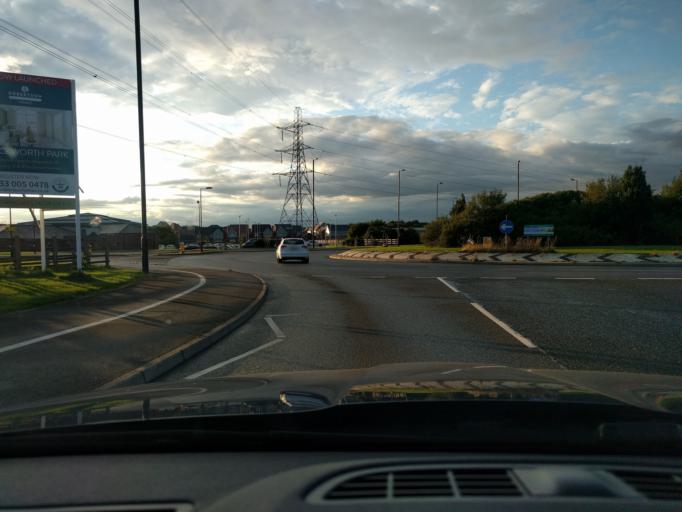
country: GB
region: England
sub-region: Northumberland
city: Backworth
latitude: 55.0339
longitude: -1.5229
